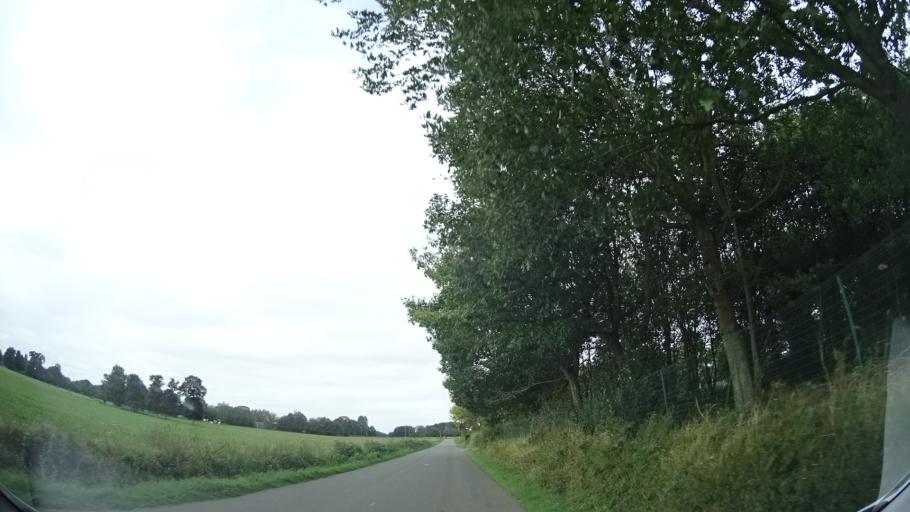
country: FR
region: Brittany
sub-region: Departement d'Ille-et-Vilaine
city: Irodouer
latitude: 48.2855
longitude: -1.9167
